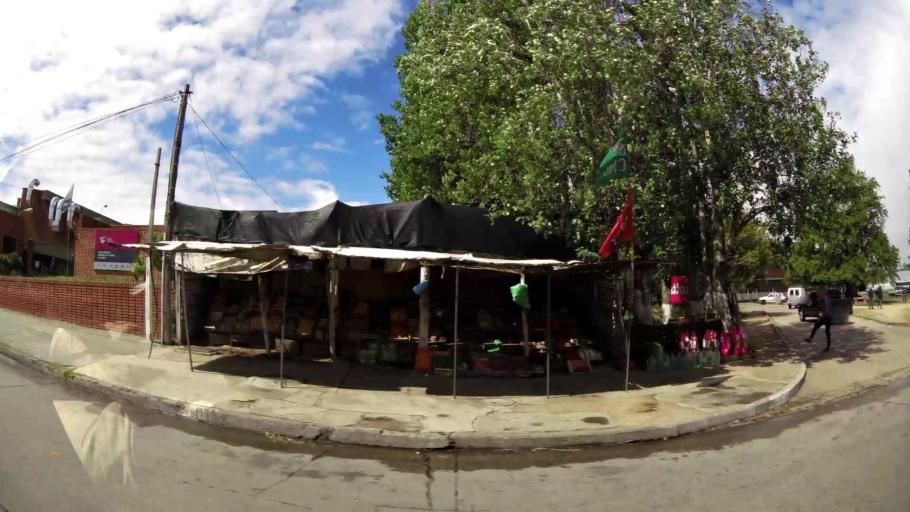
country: UY
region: Montevideo
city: Montevideo
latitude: -34.8621
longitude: -56.1702
